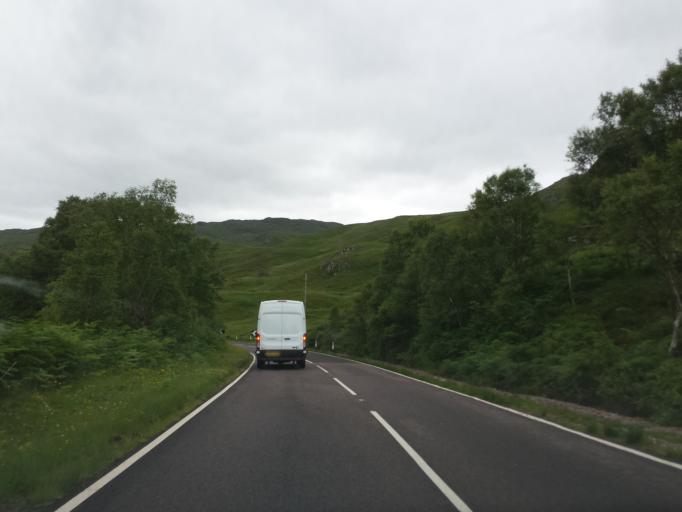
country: GB
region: Scotland
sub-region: Argyll and Bute
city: Isle Of Mull
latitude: 56.8844
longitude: -5.6149
